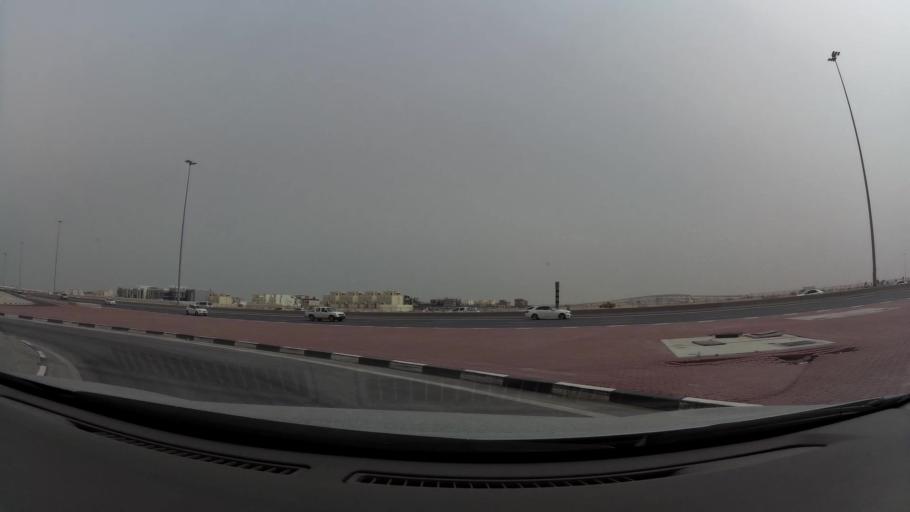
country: QA
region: Baladiyat ad Dawhah
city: Doha
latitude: 25.2219
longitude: 51.5367
